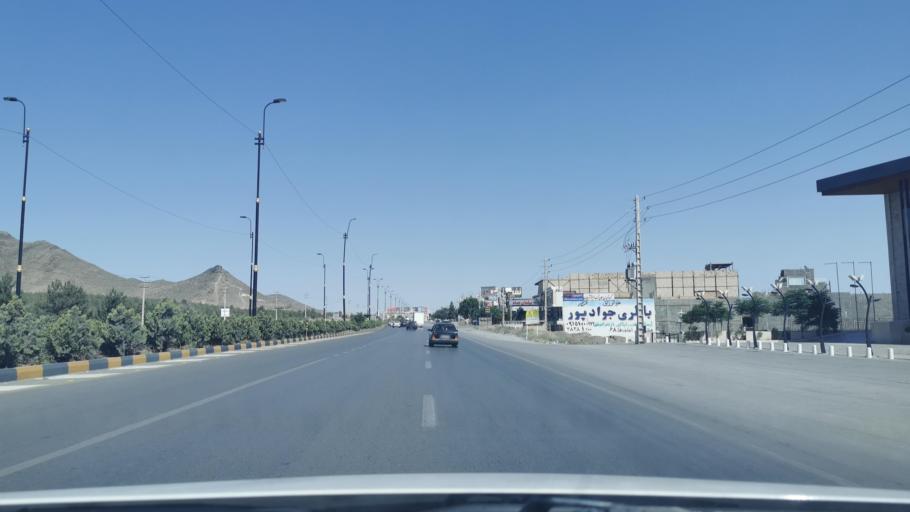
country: IR
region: Razavi Khorasan
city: Torqabeh
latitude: 36.3901
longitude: 59.4060
